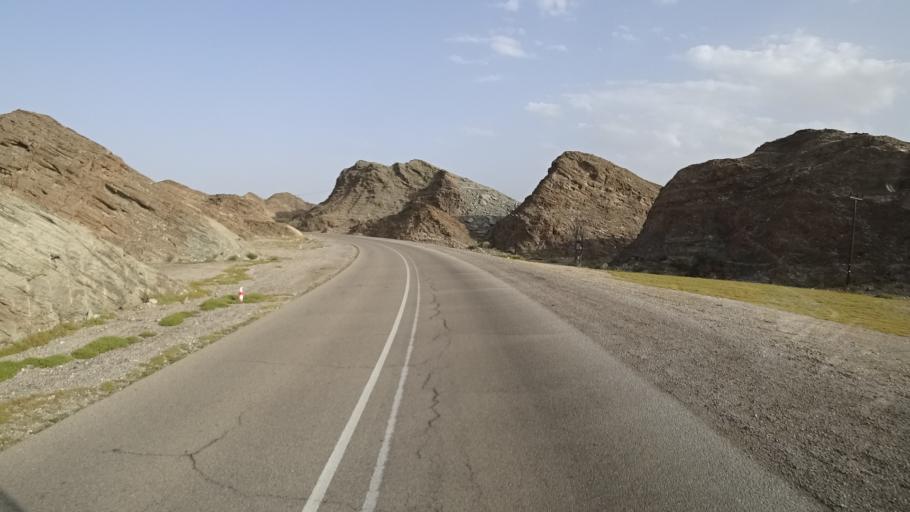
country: OM
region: Muhafazat Masqat
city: Bawshar
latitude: 23.3593
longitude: 58.5263
